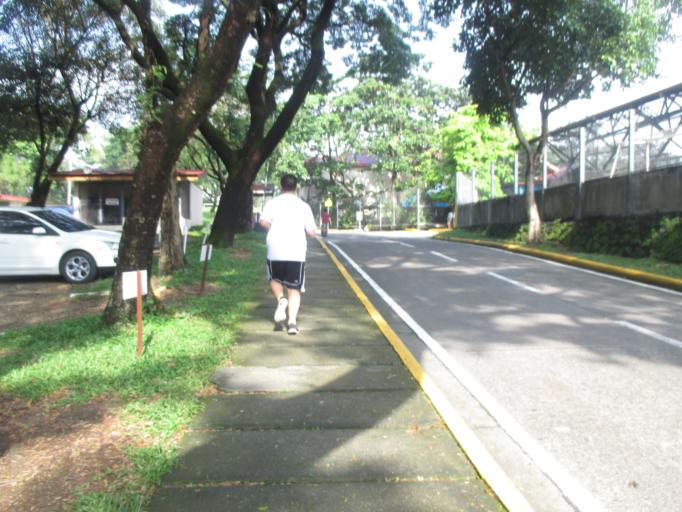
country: PH
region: Metro Manila
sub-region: Marikina
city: Calumpang
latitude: 14.6364
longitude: 121.0790
